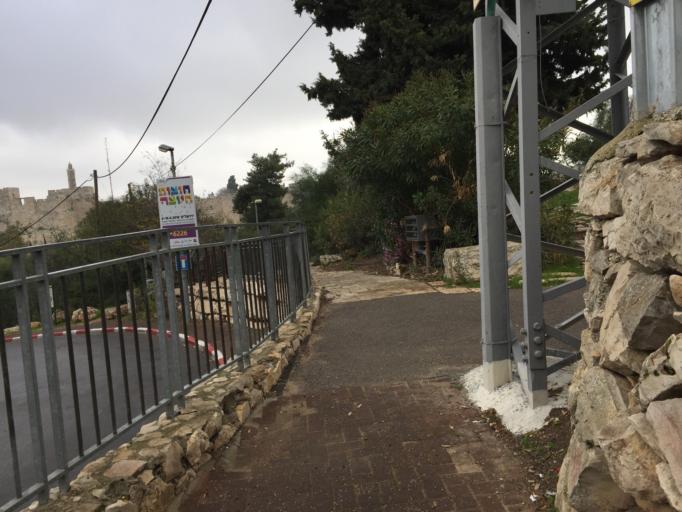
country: IL
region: Jerusalem
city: West Jerusalem
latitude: 31.7749
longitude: 35.2246
